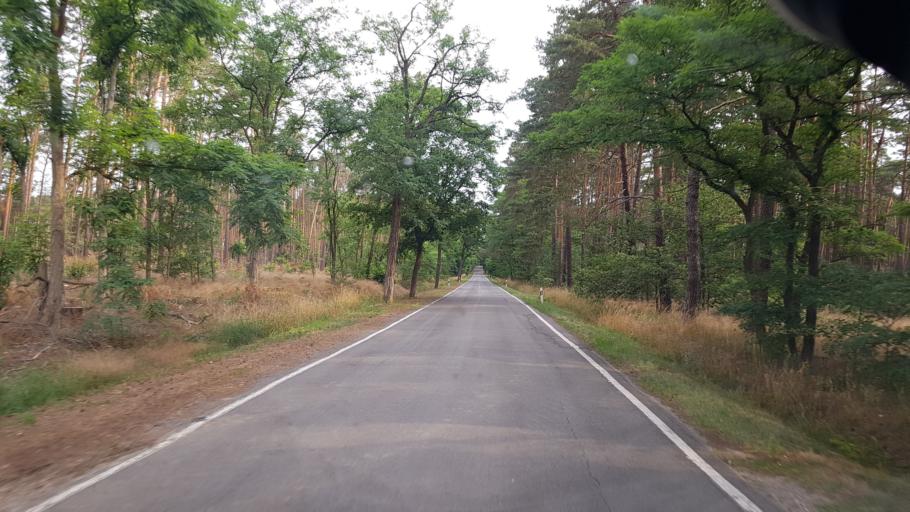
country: DE
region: Brandenburg
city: Dahme
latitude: 51.9344
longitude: 13.3968
